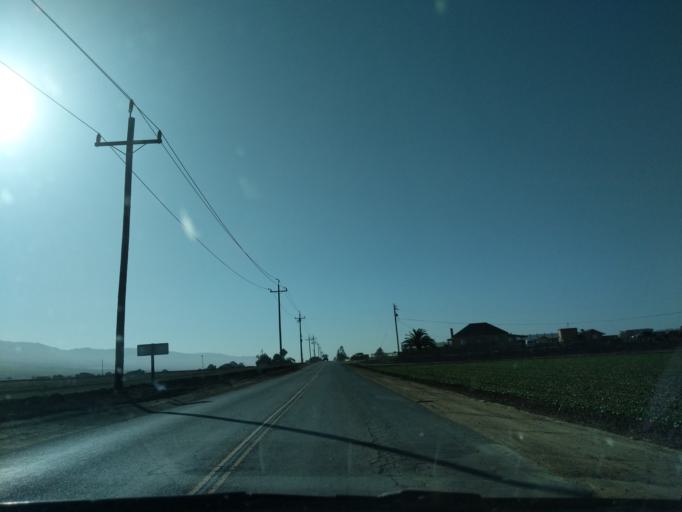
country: US
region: California
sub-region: Monterey County
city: Soledad
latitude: 36.3957
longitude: -121.3339
